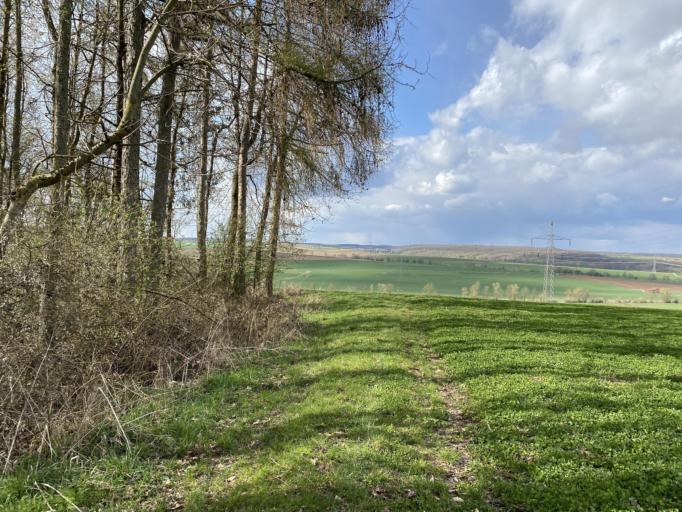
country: DE
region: Bavaria
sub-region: Regierungsbezirk Unterfranken
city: Werneck
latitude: 49.9625
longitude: 10.0662
